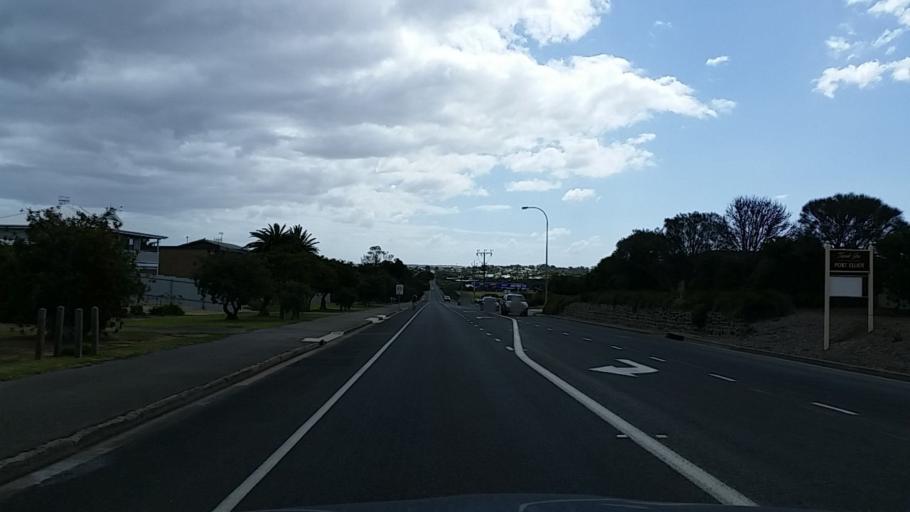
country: AU
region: South Australia
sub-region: Alexandrina
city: Port Elliot
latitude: -35.5314
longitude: 138.6733
